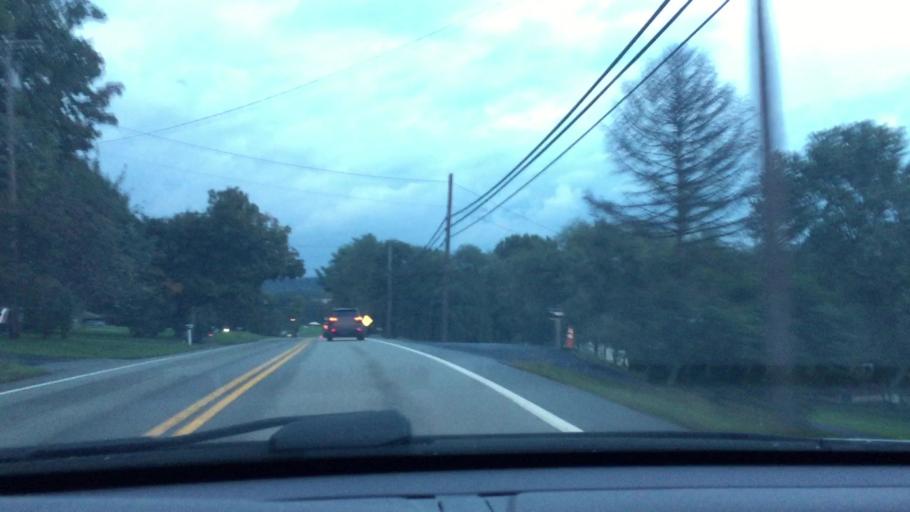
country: US
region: Pennsylvania
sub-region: Washington County
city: McGovern
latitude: 40.1852
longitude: -80.1590
